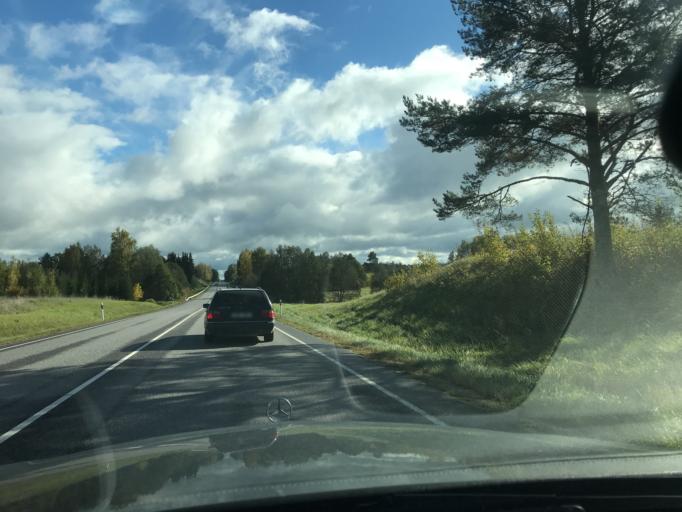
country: EE
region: Vorumaa
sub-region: Voru linn
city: Voru
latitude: 57.7801
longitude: 27.1125
